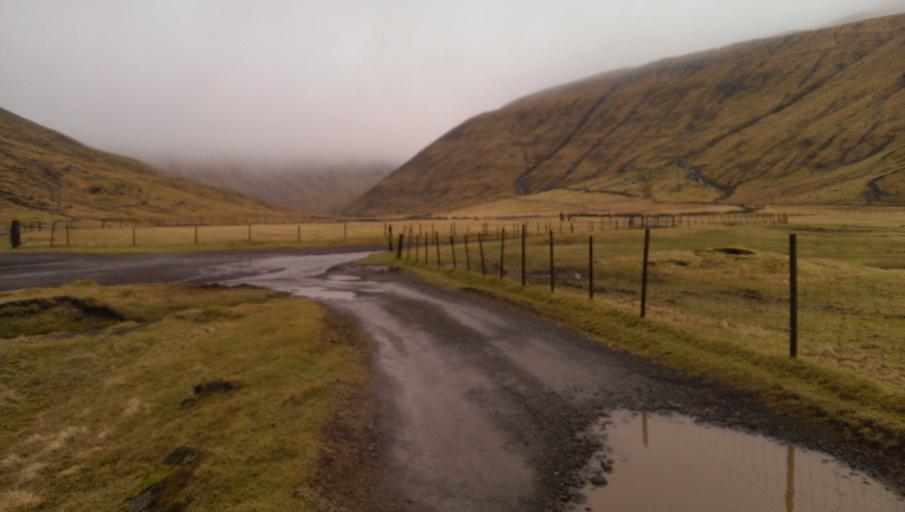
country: FO
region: Streymoy
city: Kollafjordhur
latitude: 62.1321
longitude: -7.0227
